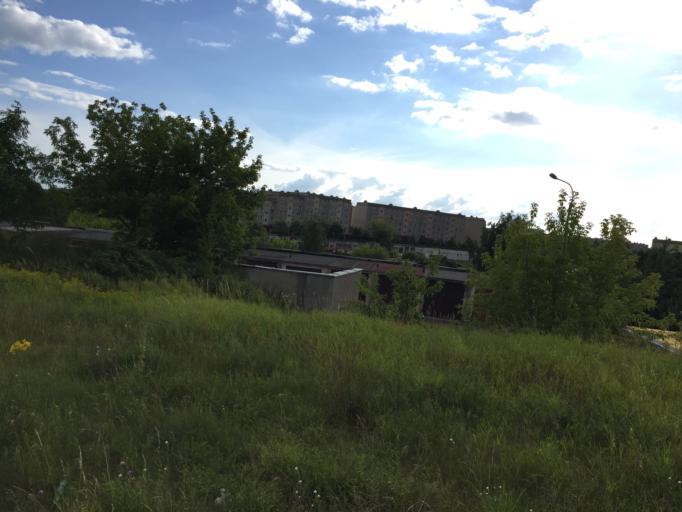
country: PL
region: Podlasie
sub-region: Suwalki
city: Suwalki
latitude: 54.1200
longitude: 22.9528
